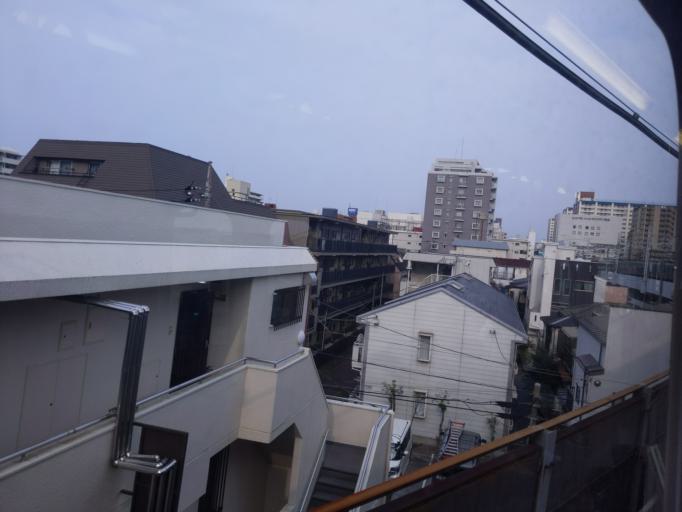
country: JP
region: Saitama
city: Shimotoda
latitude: 35.7863
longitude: 139.6783
